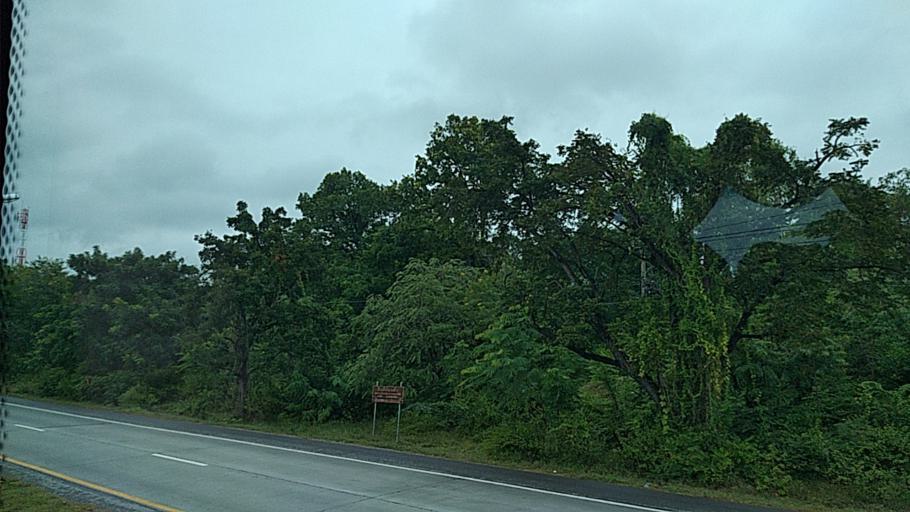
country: TH
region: Nakhon Ratchasima
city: Sida
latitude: 15.5621
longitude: 102.5517
